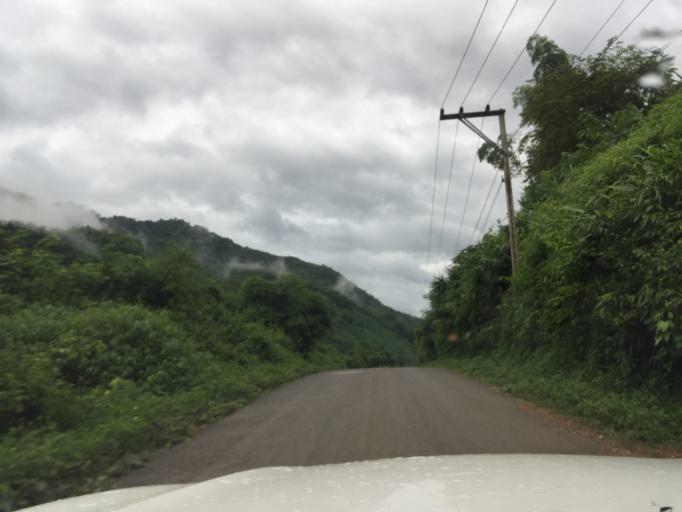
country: LA
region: Oudomxai
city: Muang La
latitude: 20.9988
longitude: 102.2321
